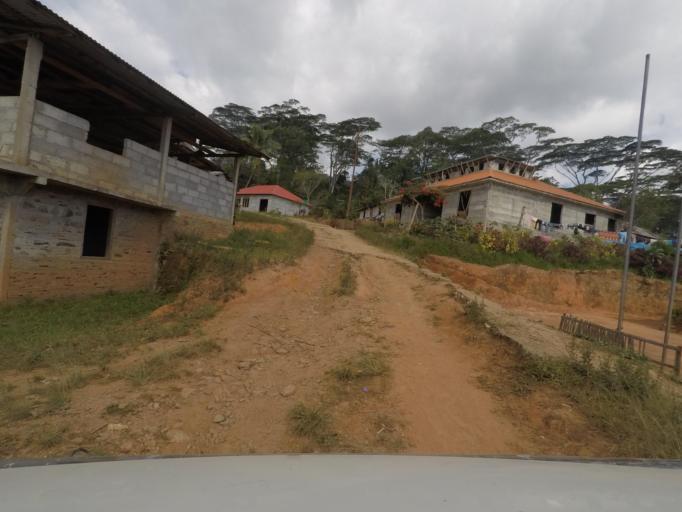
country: TL
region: Ermera
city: Gleno
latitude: -8.7193
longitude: 125.3216
